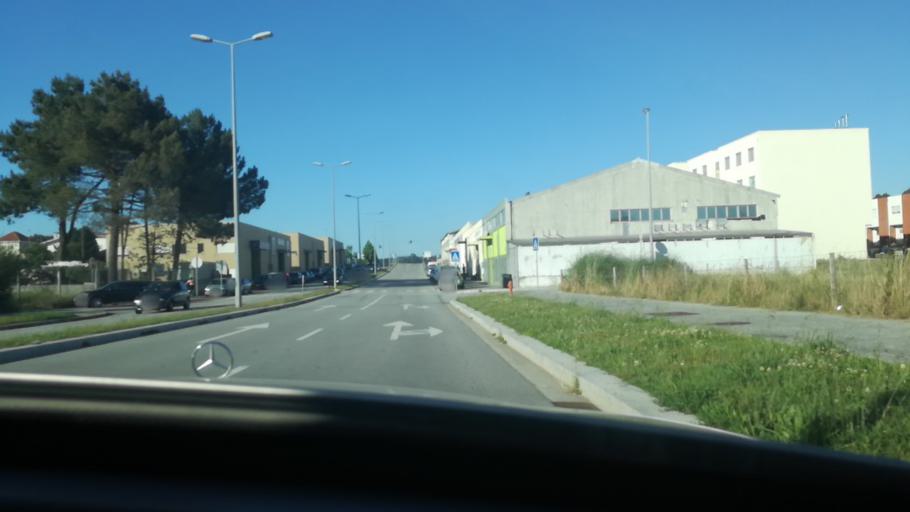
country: PT
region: Porto
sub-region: Maia
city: Maia
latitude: 41.2337
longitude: -8.6038
